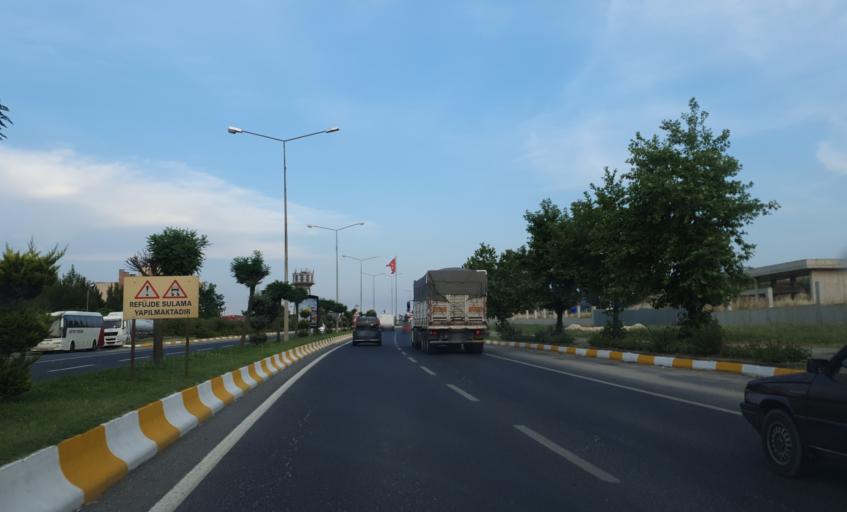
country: TR
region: Kirklareli
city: Luleburgaz
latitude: 41.4001
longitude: 27.3739
